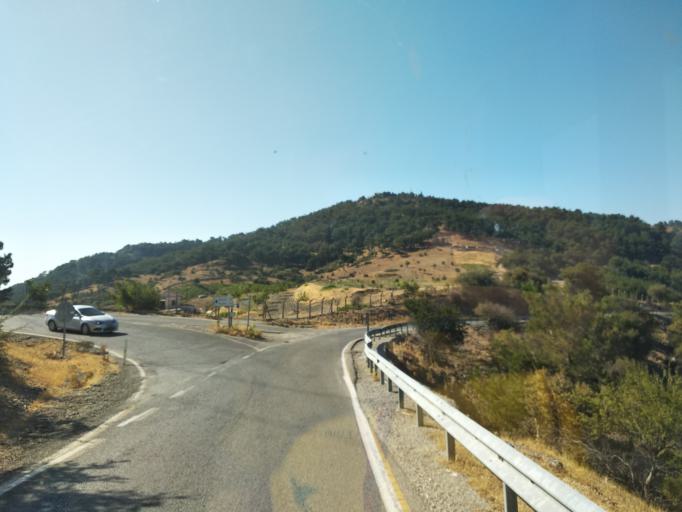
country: TR
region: Izmir
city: Gaziemir
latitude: 38.3260
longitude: 27.0041
